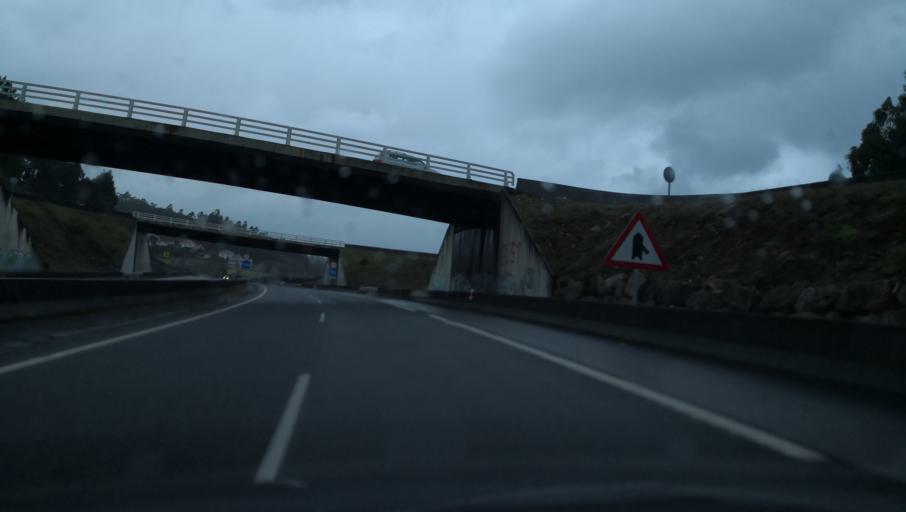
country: ES
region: Galicia
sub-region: Provincia da Coruna
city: Santiago de Compostela
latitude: 42.8369
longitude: -8.5273
